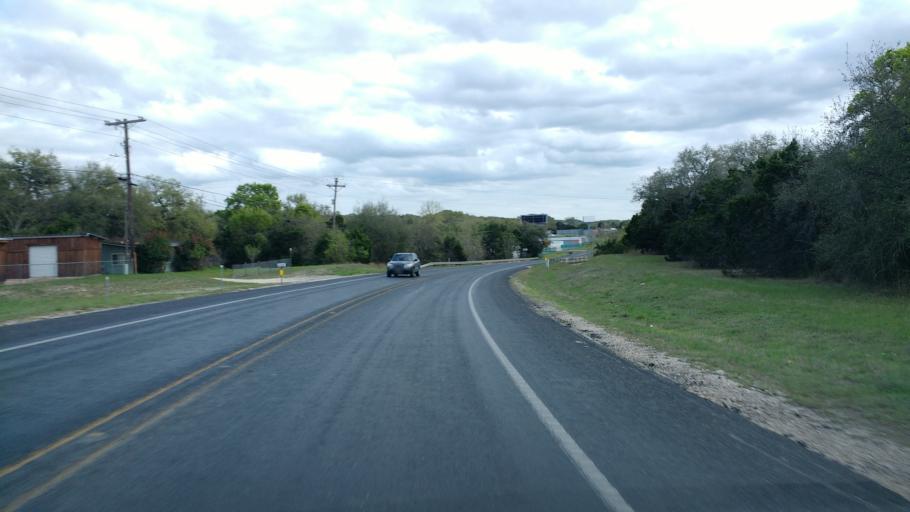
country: US
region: Texas
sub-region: Comal County
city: Canyon Lake
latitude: 29.9058
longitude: -98.2056
